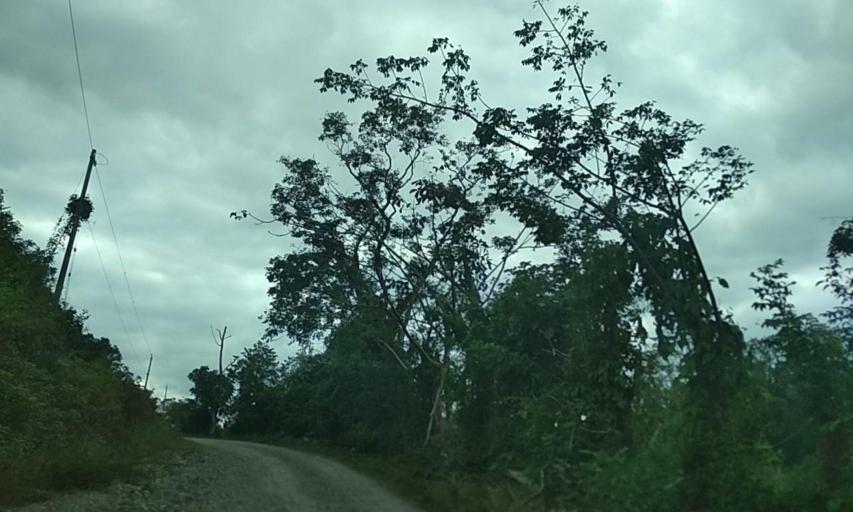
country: MX
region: Veracruz
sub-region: Papantla
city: Polutla
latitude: 20.5090
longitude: -97.2991
